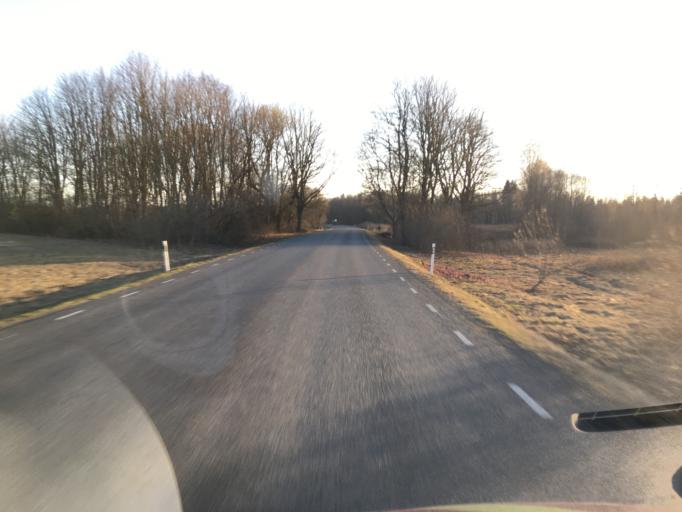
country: EE
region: Raplamaa
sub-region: Kehtna vald
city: Kehtna
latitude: 59.0381
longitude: 24.9319
